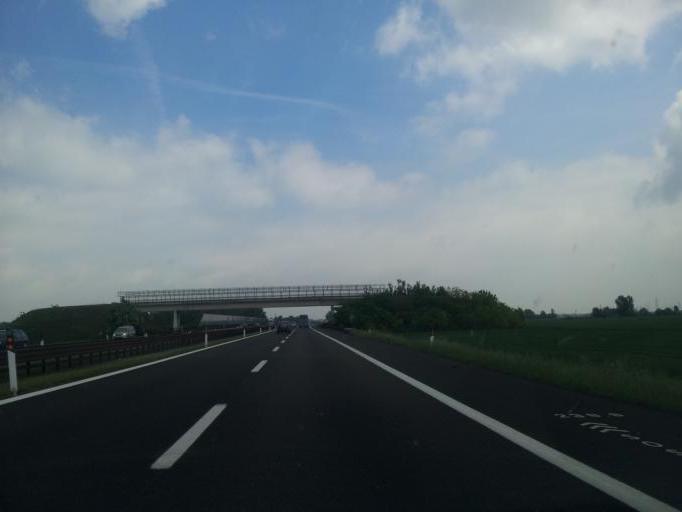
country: IT
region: Veneto
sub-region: Provincia di Verona
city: Nogarole Rocca
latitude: 45.3130
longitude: 10.9088
